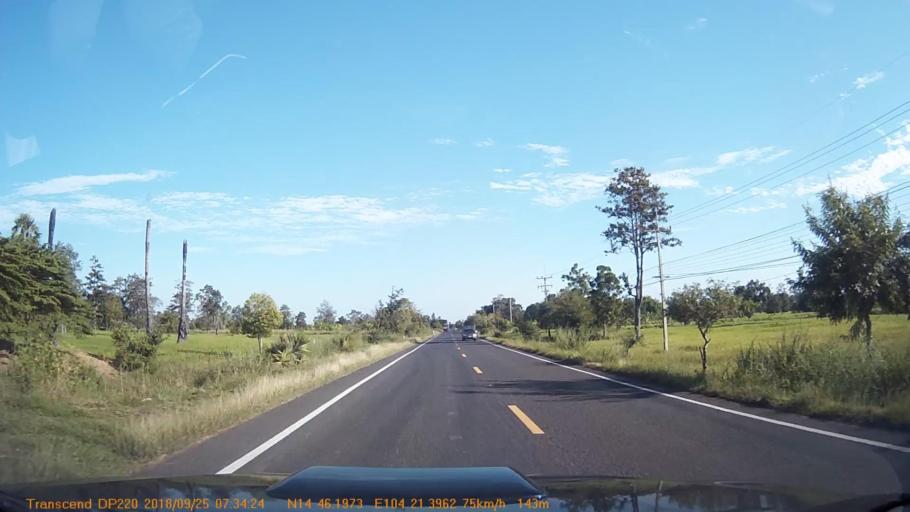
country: TH
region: Sisaket
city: Phrai Bueng
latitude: 14.7704
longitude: 104.3565
